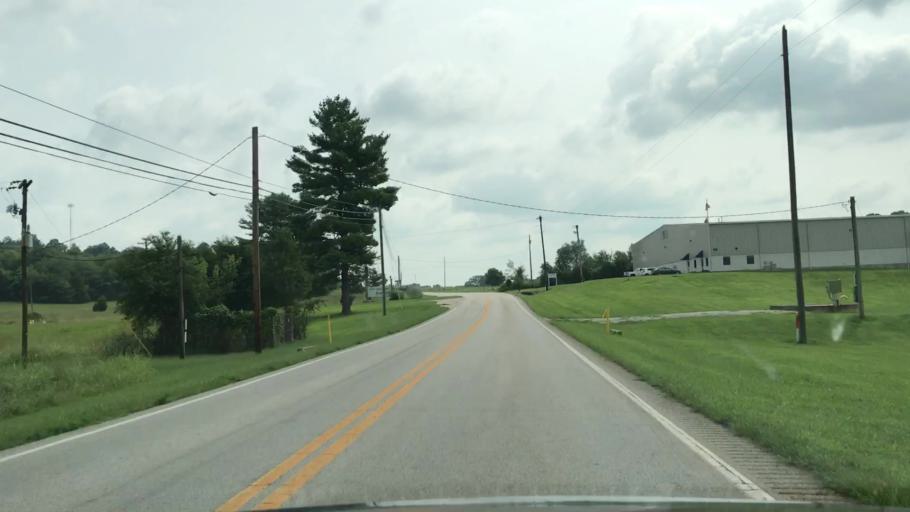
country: US
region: Kentucky
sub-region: Barren County
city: Cave City
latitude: 37.0901
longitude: -86.0731
